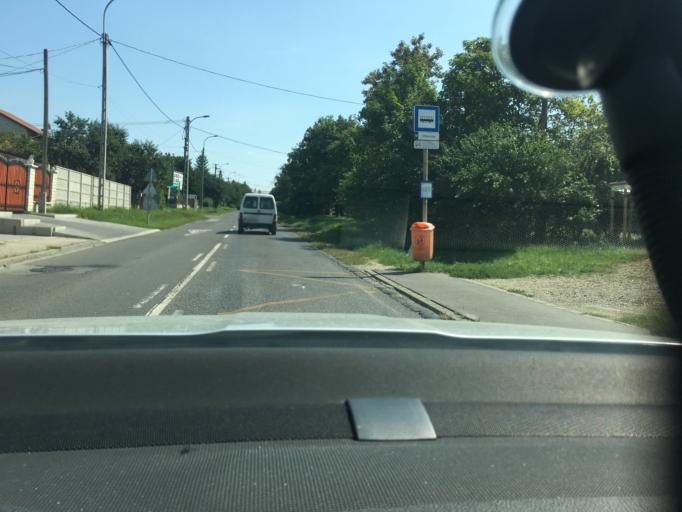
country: HU
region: Pest
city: Ecser
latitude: 47.4679
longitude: 19.3021
